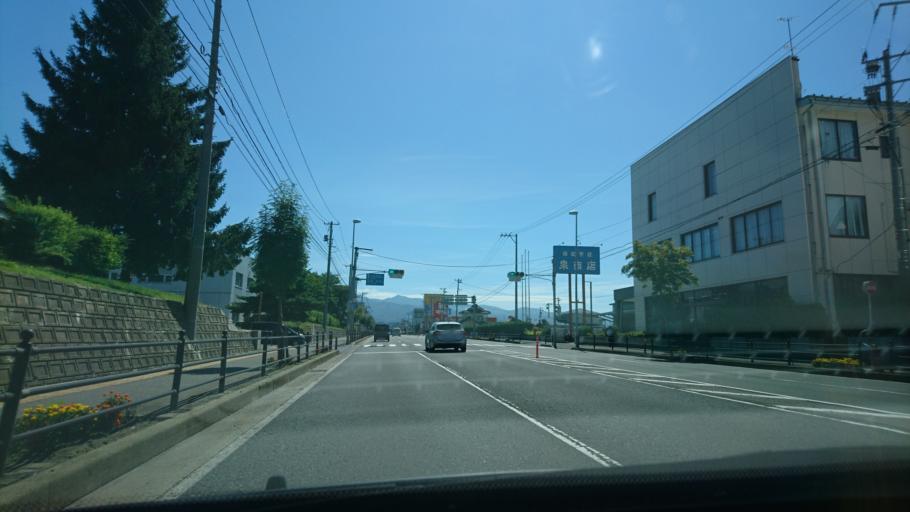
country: JP
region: Iwate
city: Tono
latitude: 39.3385
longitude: 141.5411
